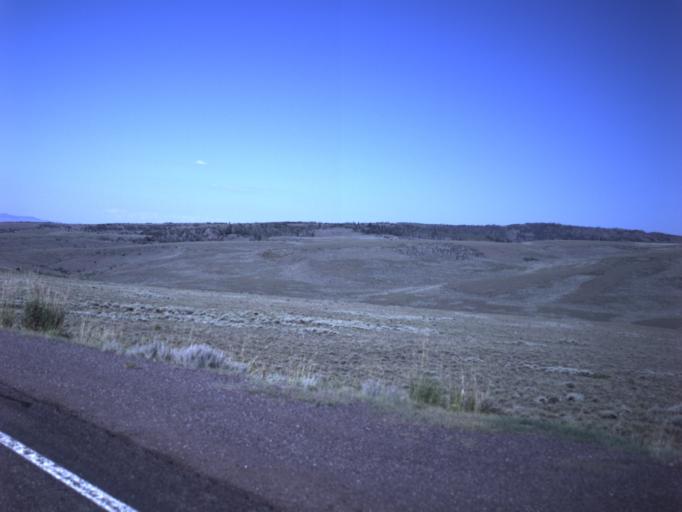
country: US
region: Utah
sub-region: Wayne County
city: Loa
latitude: 38.5689
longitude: -111.5002
